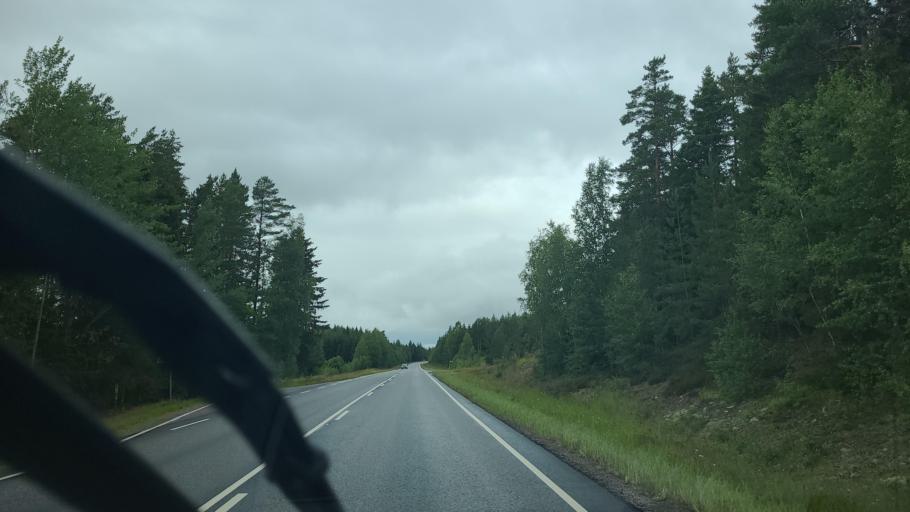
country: FI
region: Varsinais-Suomi
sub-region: Aboland-Turunmaa
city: Kimito
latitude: 60.2052
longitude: 22.6474
